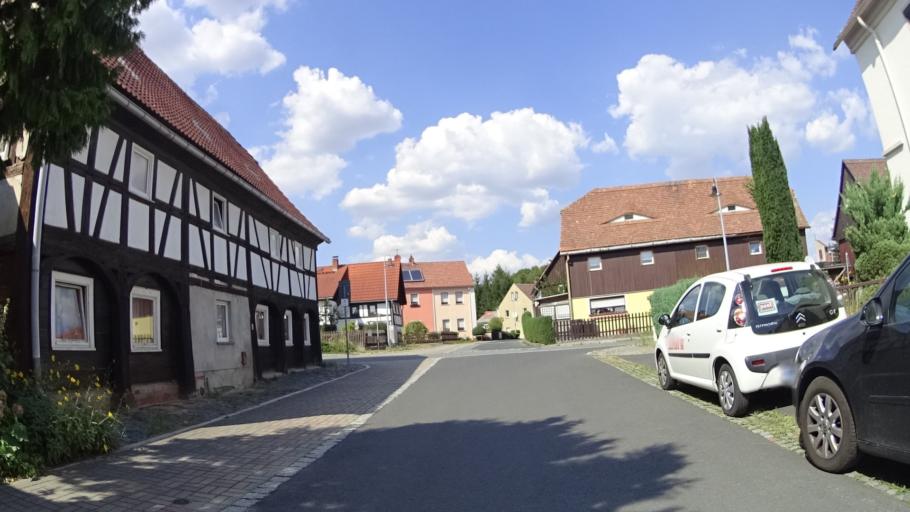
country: DE
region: Saxony
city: Hirschfelde
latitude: 50.9442
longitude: 14.8847
